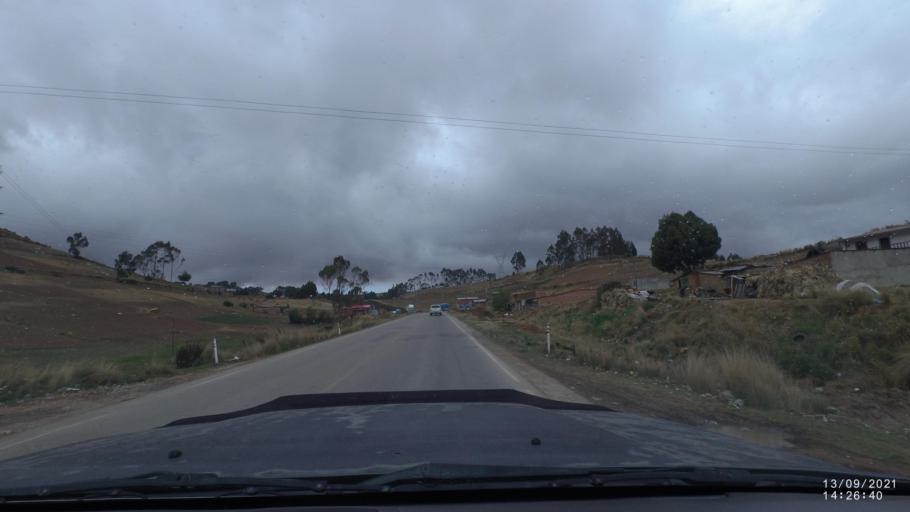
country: BO
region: Cochabamba
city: Colomi
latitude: -17.3087
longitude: -65.8662
